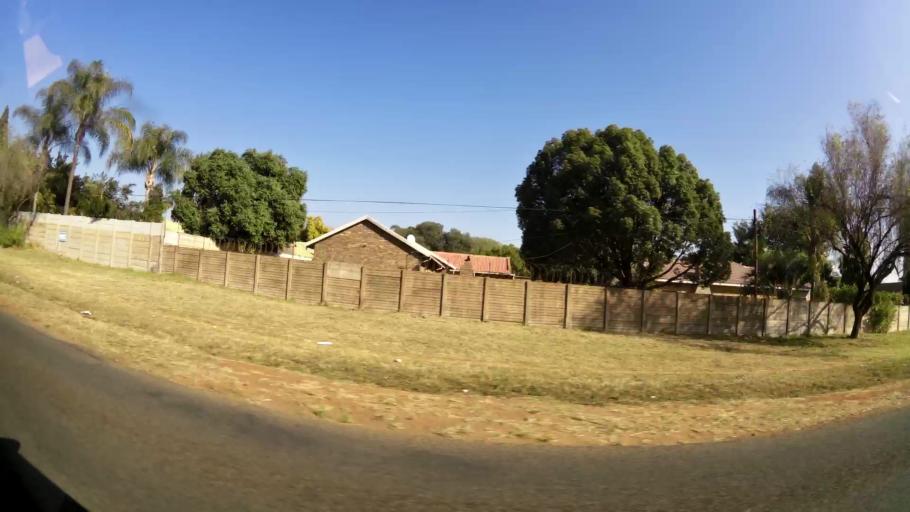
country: ZA
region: Gauteng
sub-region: City of Tshwane Metropolitan Municipality
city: Pretoria
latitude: -25.6525
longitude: 28.2445
